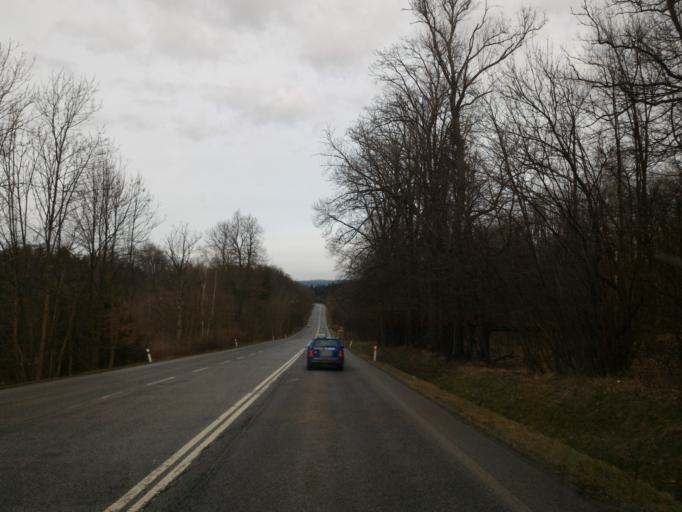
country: CZ
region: Ustecky
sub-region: Okres Decin
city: Rumburk
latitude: 50.9171
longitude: 14.5646
